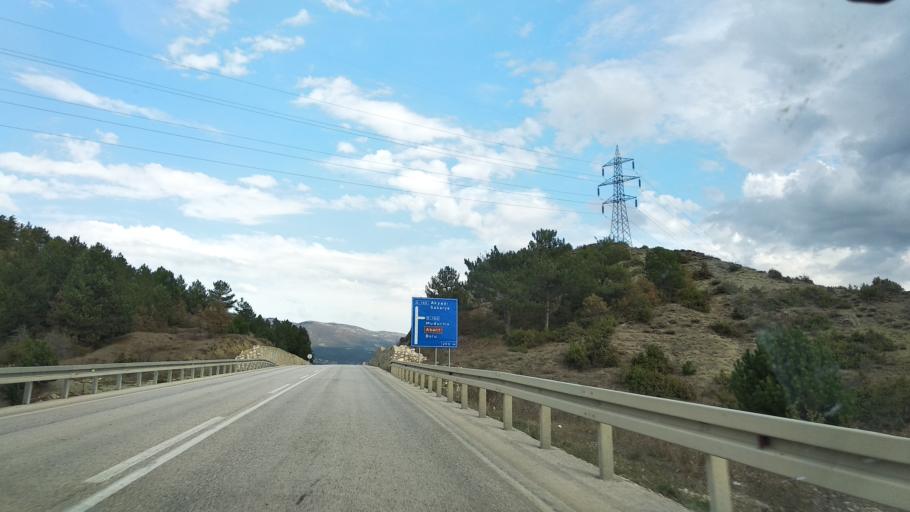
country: TR
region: Bolu
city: Mudurnu
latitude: 40.4756
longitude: 31.1564
